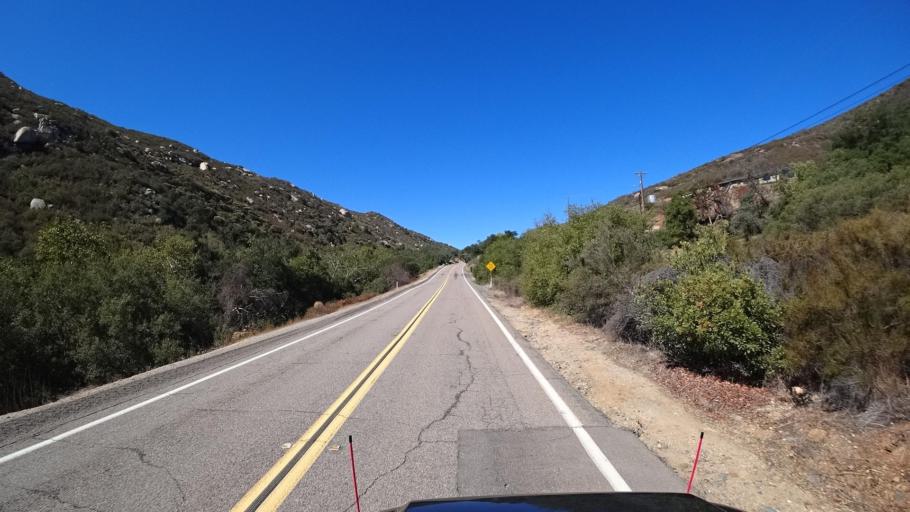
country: US
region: California
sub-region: San Diego County
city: Alpine
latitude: 32.7050
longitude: -116.7290
